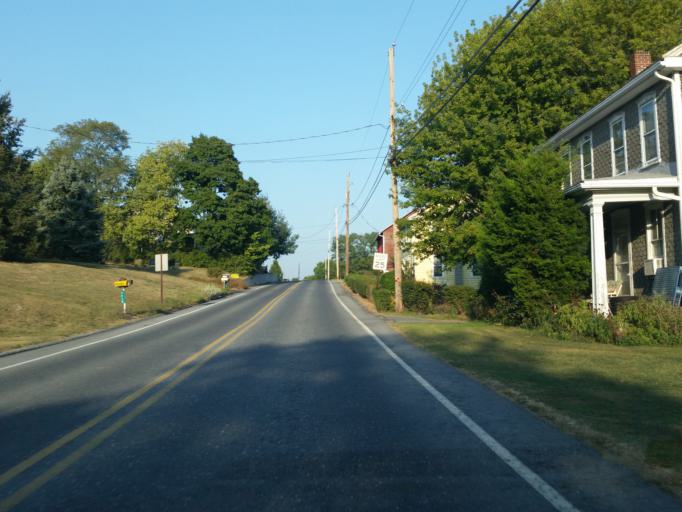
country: US
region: Pennsylvania
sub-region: Lebanon County
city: Annville
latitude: 40.3389
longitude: -76.5340
